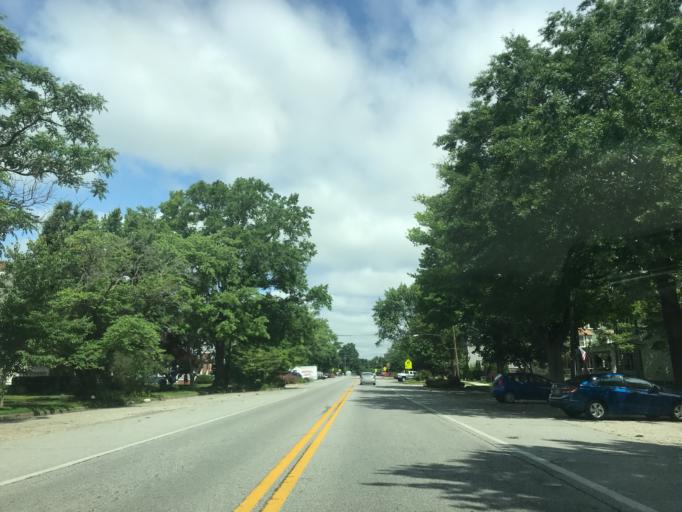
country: US
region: Maryland
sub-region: Caroline County
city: Ridgely
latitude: 38.9451
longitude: -75.8828
